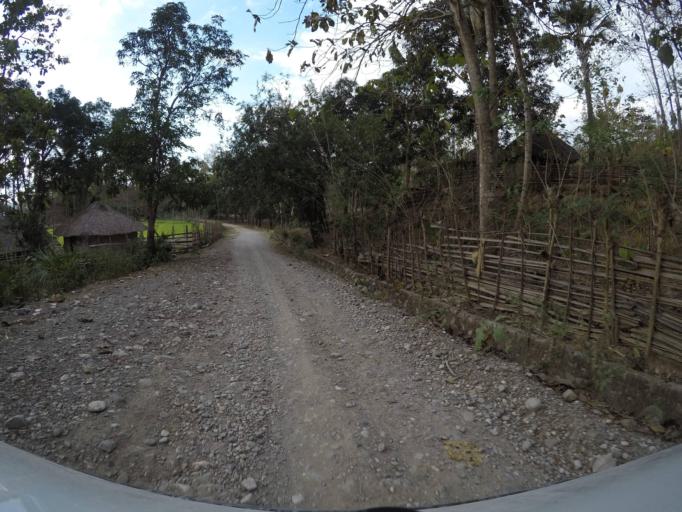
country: TL
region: Bobonaro
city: Maliana
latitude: -8.8915
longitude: 125.2103
